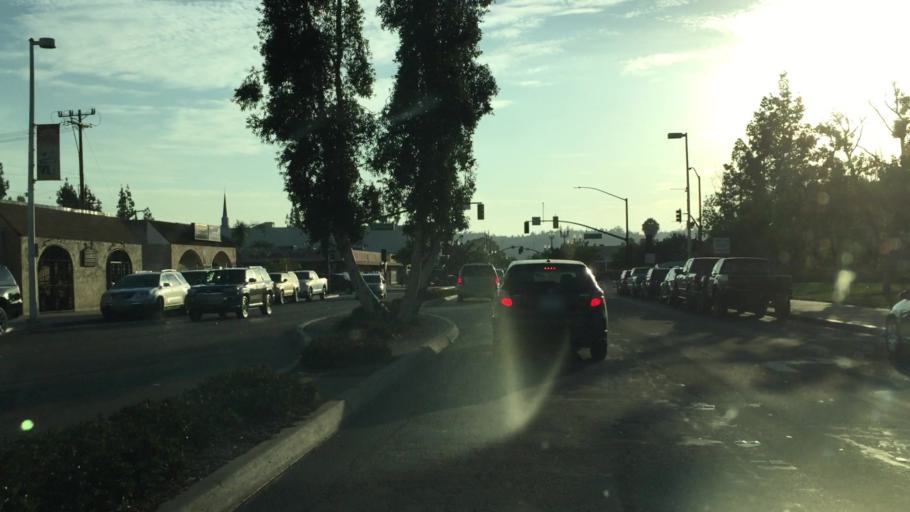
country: US
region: California
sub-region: San Diego County
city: El Cajon
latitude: 32.7950
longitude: -116.9580
